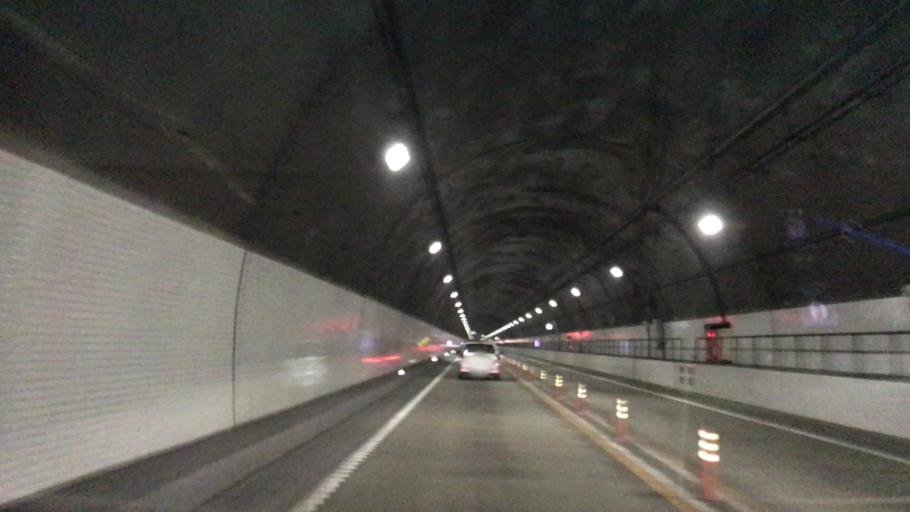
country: JP
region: Hokkaido
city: Shimo-furano
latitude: 42.9647
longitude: 142.3627
